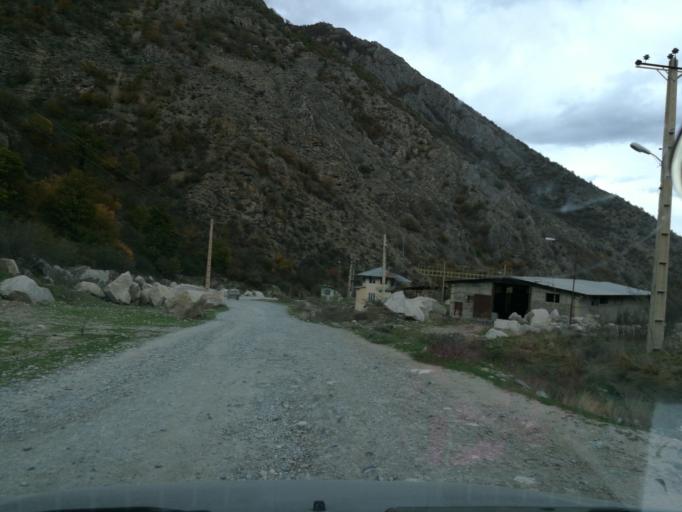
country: IR
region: Mazandaran
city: `Abbasabad
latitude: 36.4473
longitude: 51.0629
